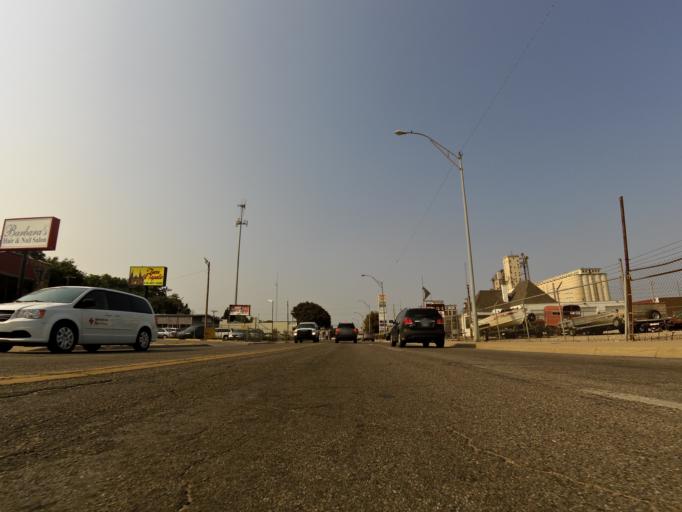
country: US
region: Kansas
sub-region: Sedgwick County
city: Wichita
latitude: 37.7138
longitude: -97.3355
